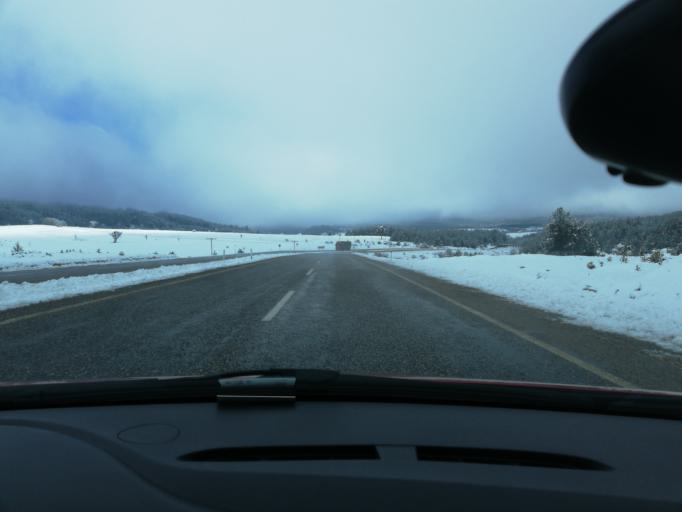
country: TR
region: Kastamonu
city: Ihsangazi
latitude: 41.3036
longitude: 33.5603
